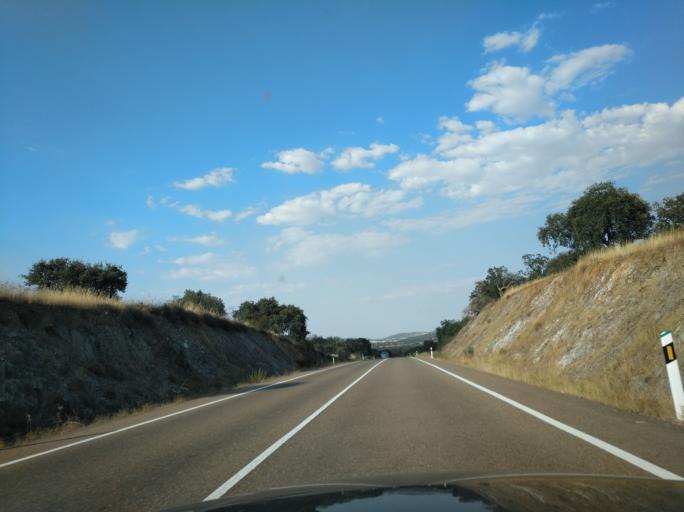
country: ES
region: Extremadura
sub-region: Provincia de Badajoz
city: Alconchel
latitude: 38.4491
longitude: -7.0863
